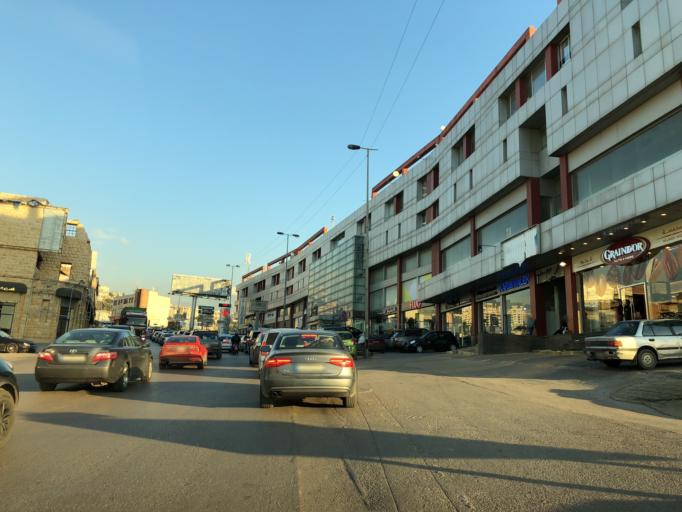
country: LB
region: Mont-Liban
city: Baabda
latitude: 33.8604
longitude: 35.5520
